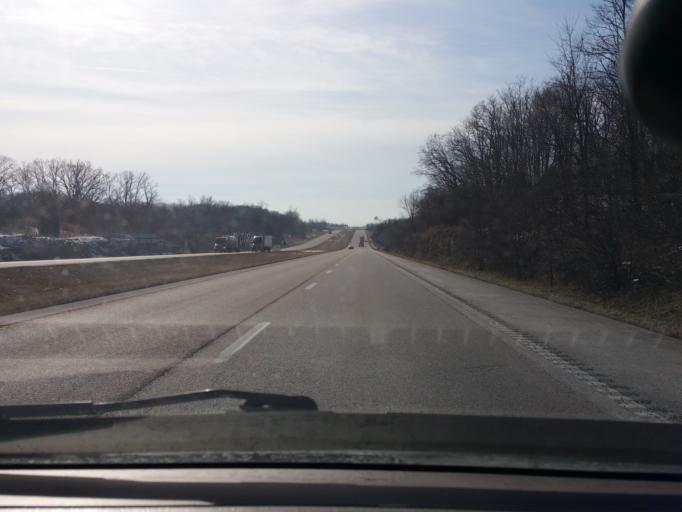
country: US
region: Missouri
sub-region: Clinton County
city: Lathrop
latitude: 39.4733
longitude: -94.3126
